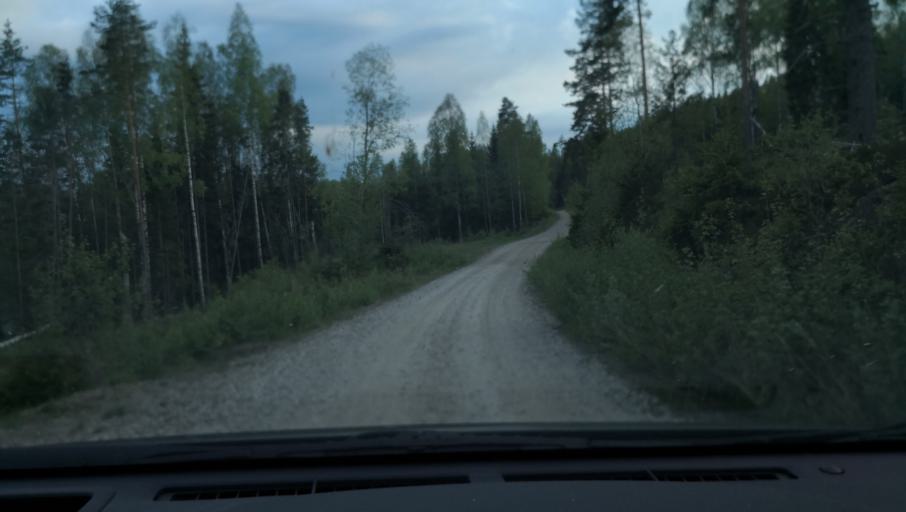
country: SE
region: Vaestmanland
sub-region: Skinnskattebergs Kommun
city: Skinnskatteberg
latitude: 59.7984
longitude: 15.4730
